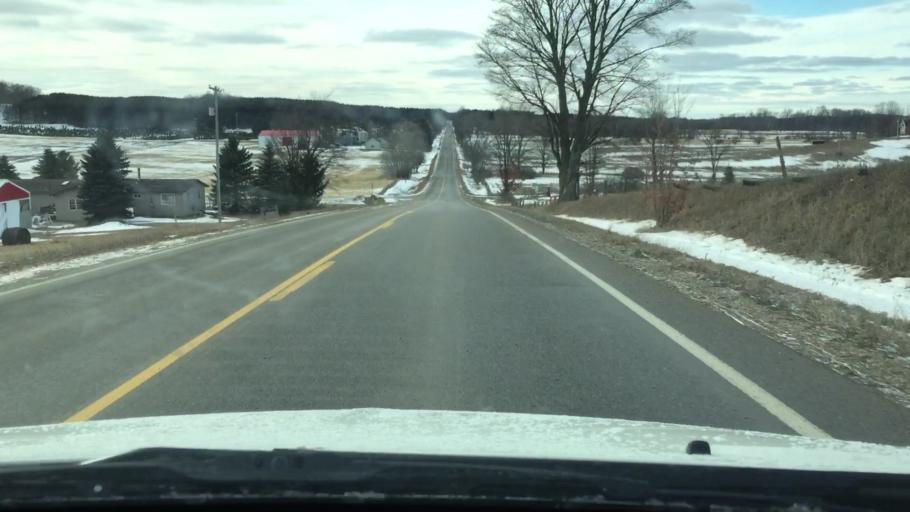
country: US
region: Michigan
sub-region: Wexford County
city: Manton
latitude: 44.4037
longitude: -85.4165
